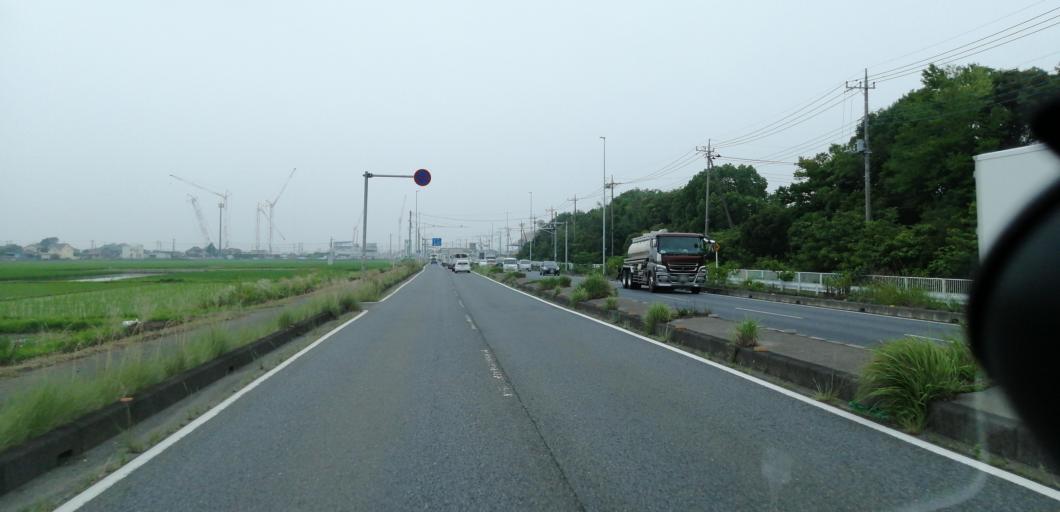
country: JP
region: Saitama
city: Hanyu
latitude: 36.1501
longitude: 139.5346
